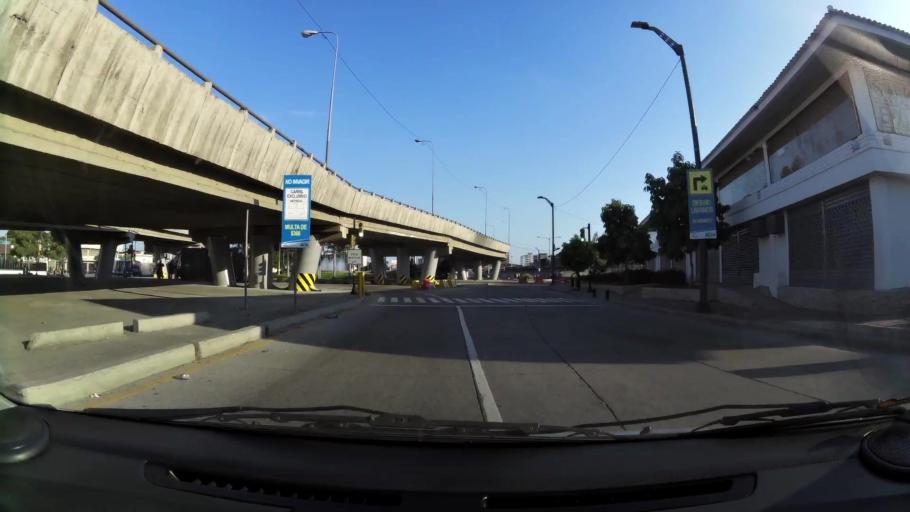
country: EC
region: Guayas
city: Guayaquil
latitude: -2.1808
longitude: -79.8924
